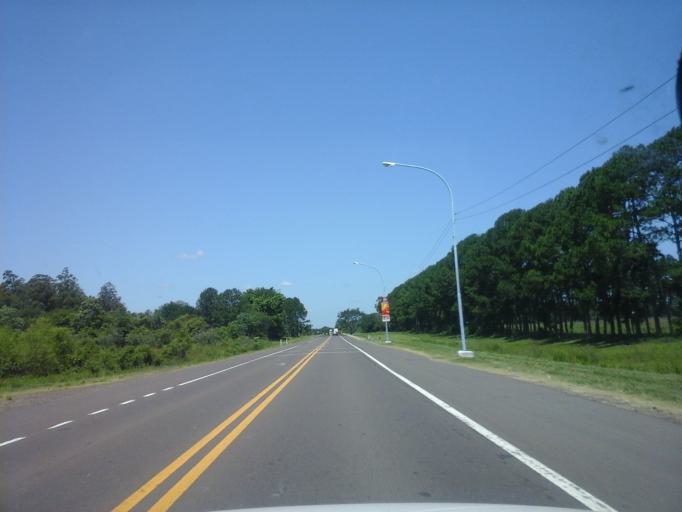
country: AR
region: Corrientes
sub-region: Departamento de San Cosme
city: San Cosme
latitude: -27.3728
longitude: -58.4857
